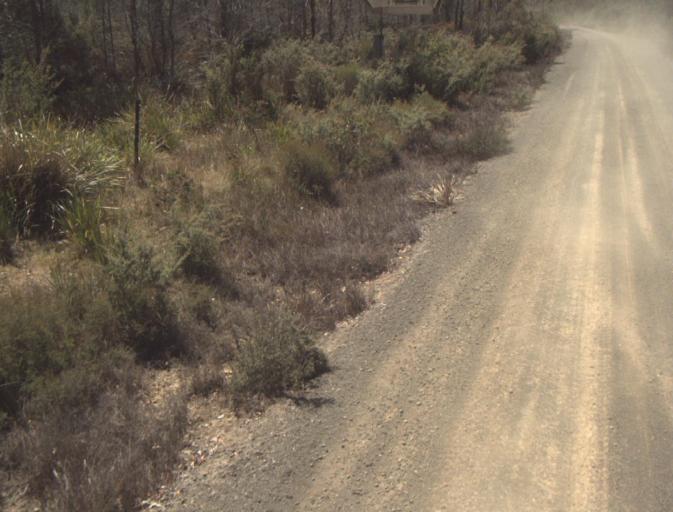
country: AU
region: Tasmania
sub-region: Launceston
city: Mayfield
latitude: -41.2791
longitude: 147.0962
